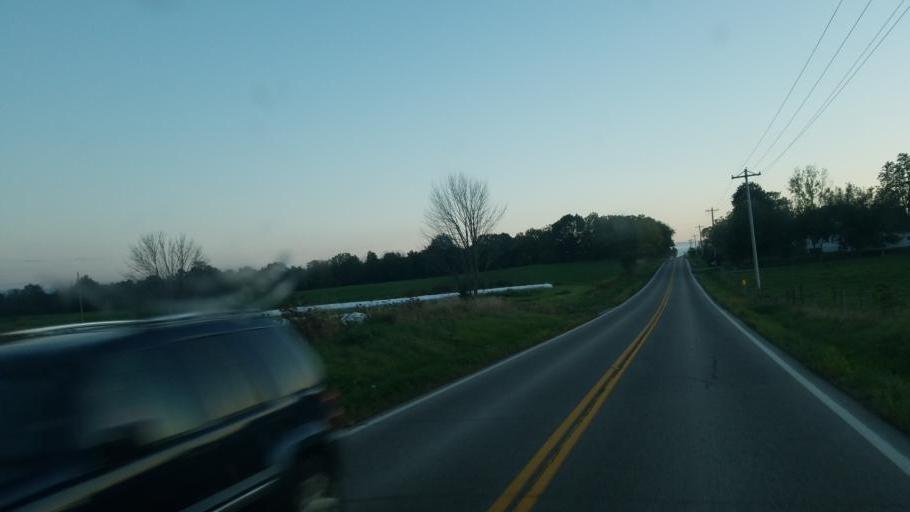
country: US
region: Ohio
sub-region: Ashland County
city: Ashland
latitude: 40.9299
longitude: -82.3952
